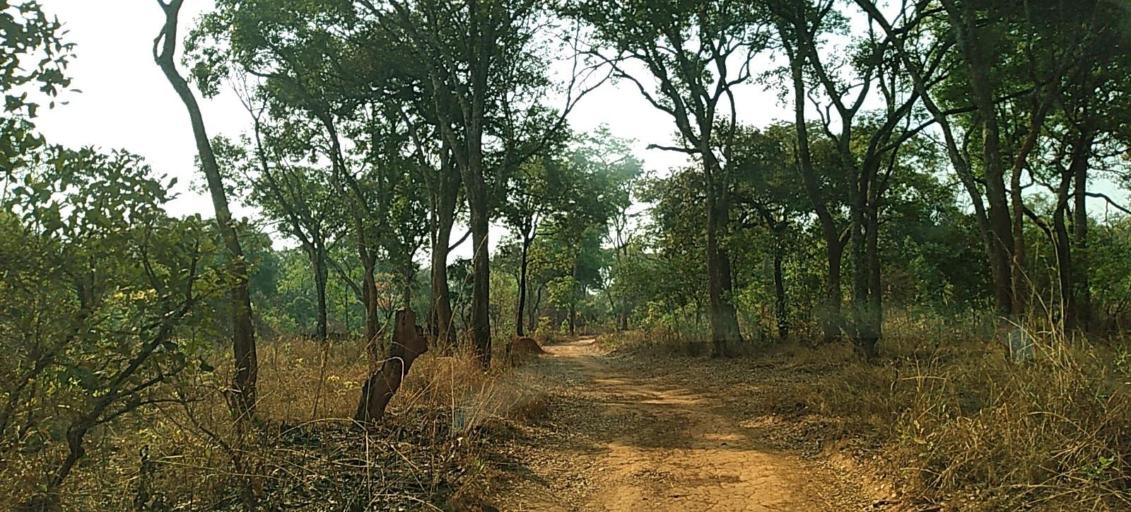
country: ZM
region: North-Western
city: Solwezi
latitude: -12.0634
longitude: 26.1745
